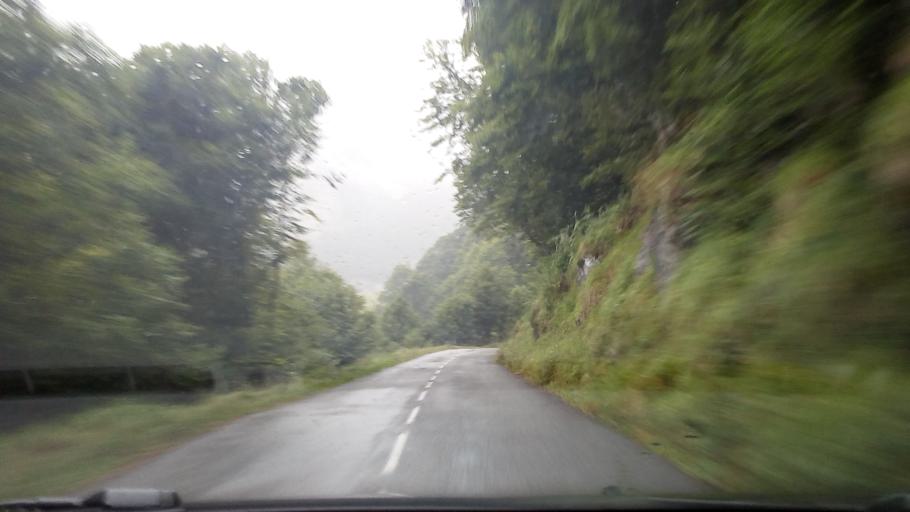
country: FR
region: Aquitaine
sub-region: Departement des Pyrenees-Atlantiques
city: Laruns
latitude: 42.9691
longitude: -0.3011
